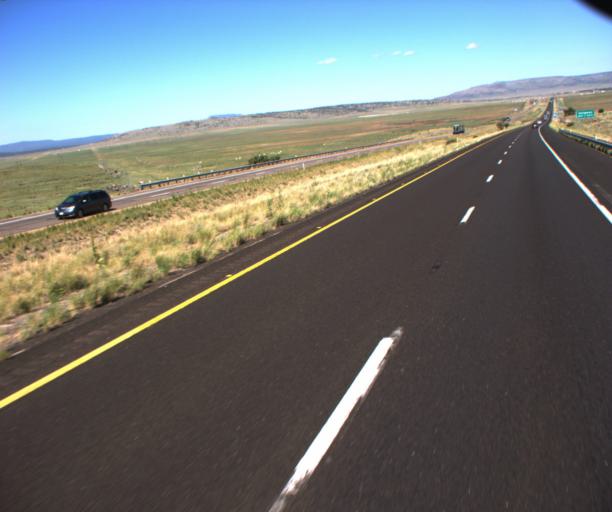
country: US
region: Arizona
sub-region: Yavapai County
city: Paulden
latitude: 35.2944
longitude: -112.8275
